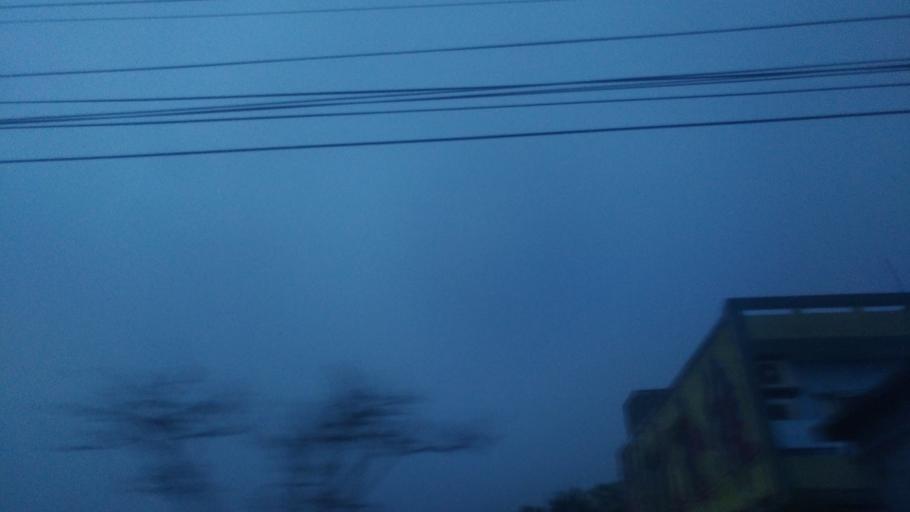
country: TW
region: Taiwan
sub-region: Miaoli
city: Miaoli
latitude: 24.5396
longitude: 120.6961
